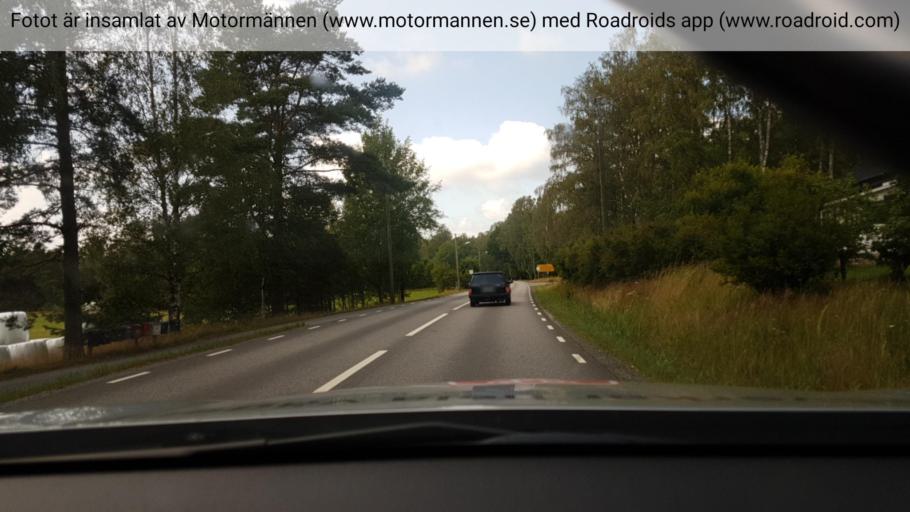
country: SE
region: Vaestra Goetaland
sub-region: Marks Kommun
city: Kinna
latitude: 57.4755
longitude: 12.7141
